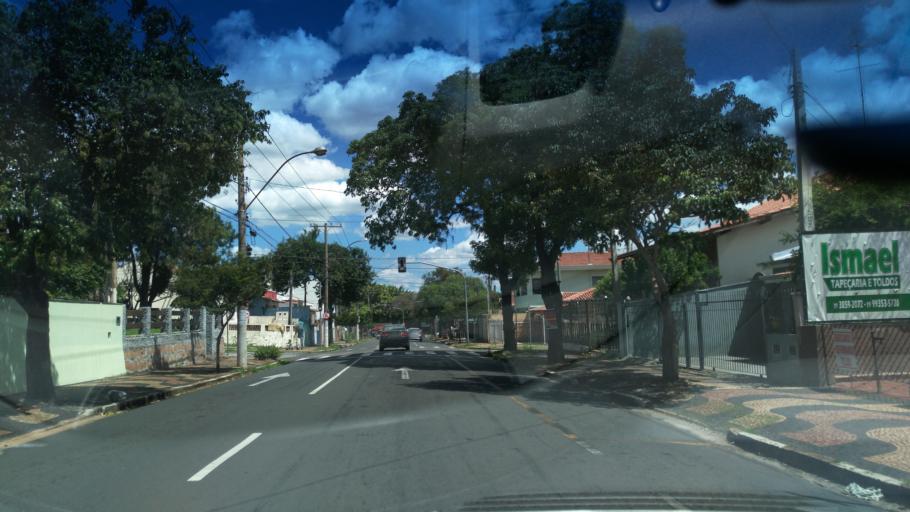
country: BR
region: Sao Paulo
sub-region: Valinhos
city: Valinhos
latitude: -22.9646
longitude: -46.9912
